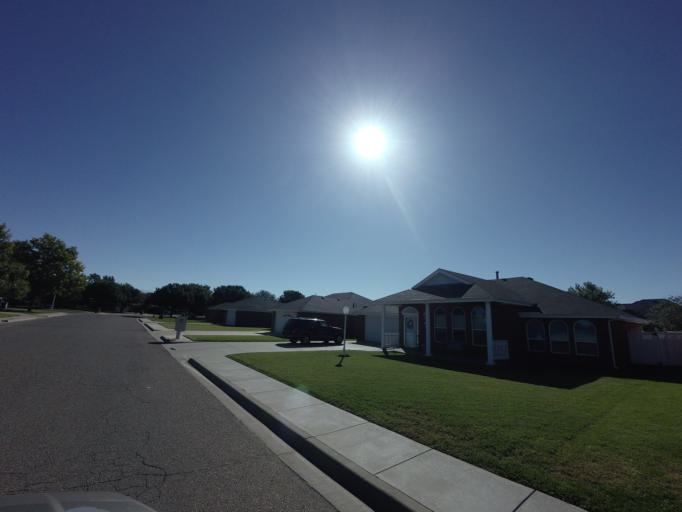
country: US
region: New Mexico
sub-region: Curry County
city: Clovis
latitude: 34.4298
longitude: -103.1777
